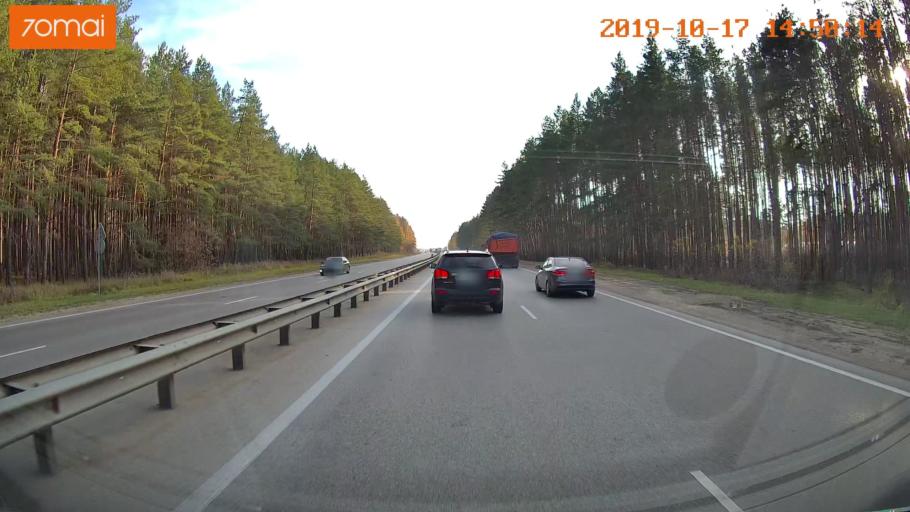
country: RU
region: Rjazan
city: Polyany
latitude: 54.7366
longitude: 39.8414
